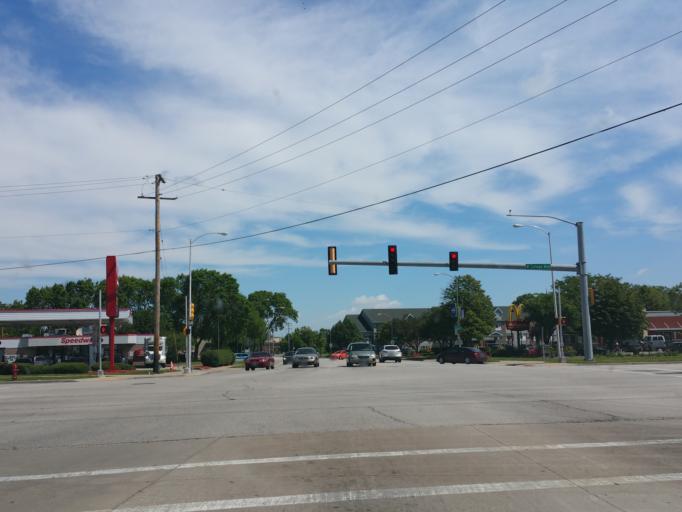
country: US
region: Wisconsin
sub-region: Milwaukee County
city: Saint Francis
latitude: 42.9301
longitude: -87.9300
